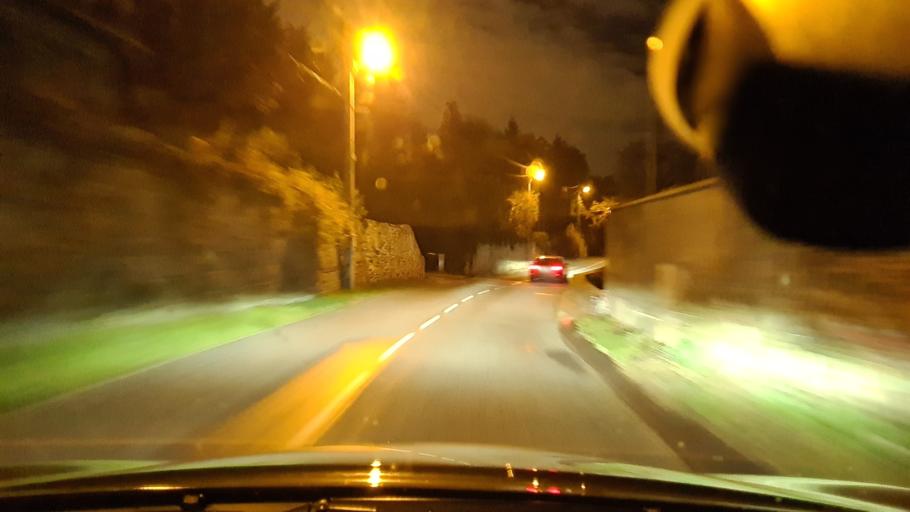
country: FR
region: Rhone-Alpes
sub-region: Departement du Rhone
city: Limonest
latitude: 45.8253
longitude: 4.7884
